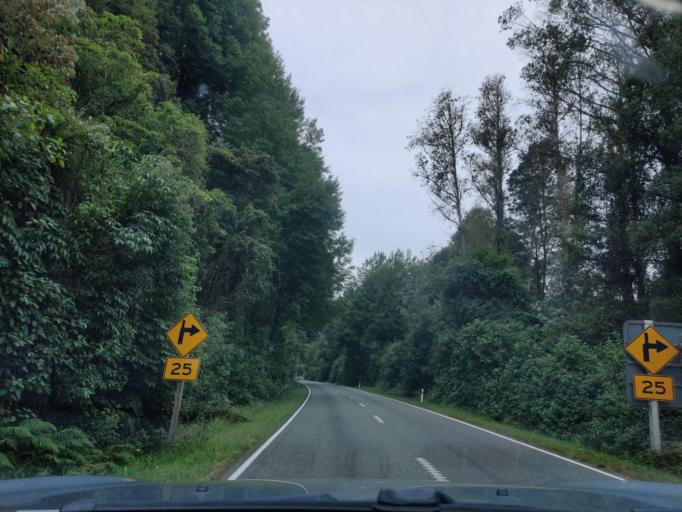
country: NZ
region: West Coast
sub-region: Buller District
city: Westport
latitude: -41.7791
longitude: 172.2150
